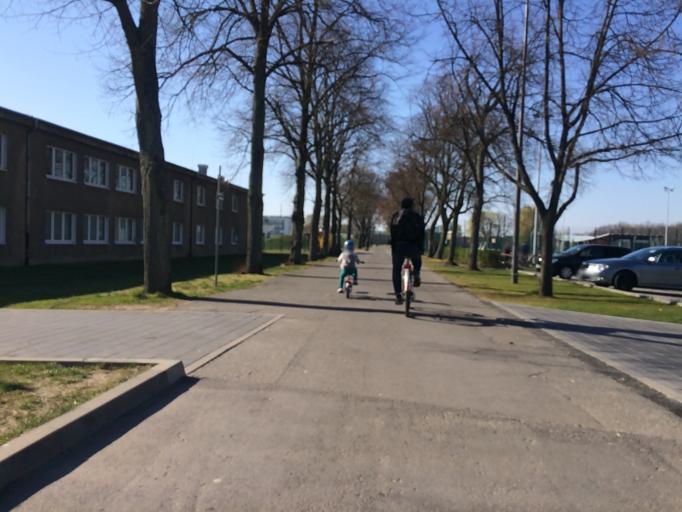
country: DE
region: Berlin
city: Fennpfuhl
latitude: 52.5402
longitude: 13.4792
